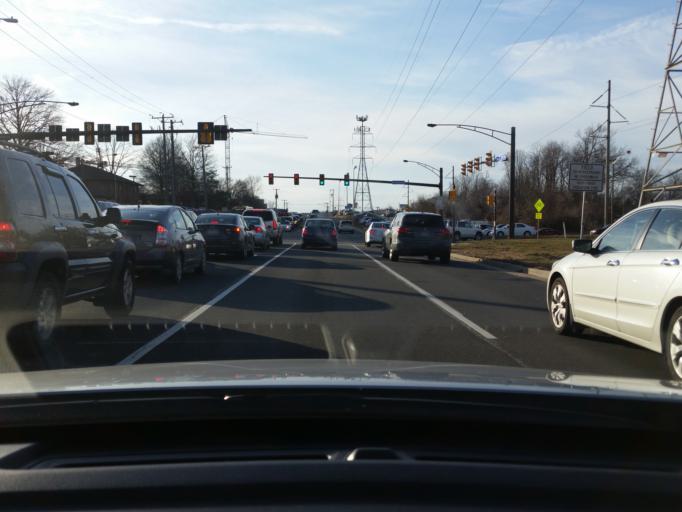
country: US
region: Virginia
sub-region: Fairfax County
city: Reston
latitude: 38.9499
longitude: -77.3352
